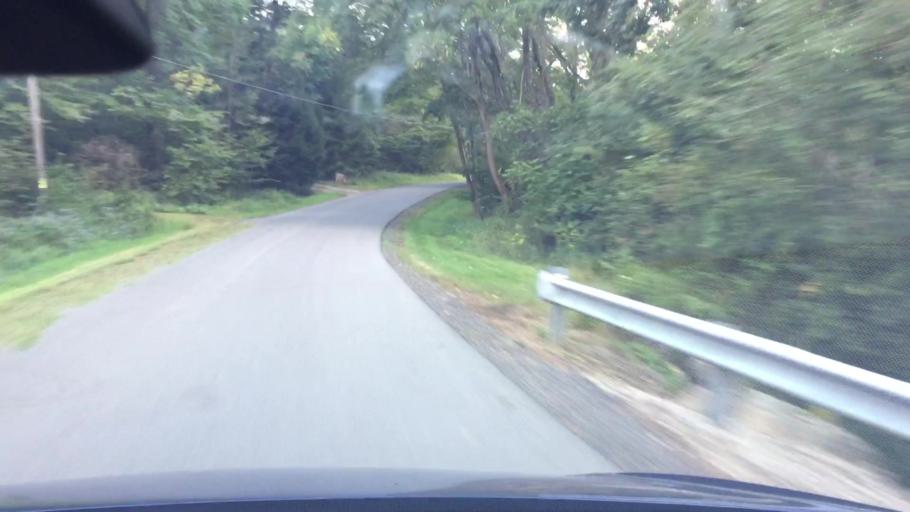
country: US
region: Pennsylvania
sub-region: Butler County
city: Oak Hills
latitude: 40.7910
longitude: -79.8867
